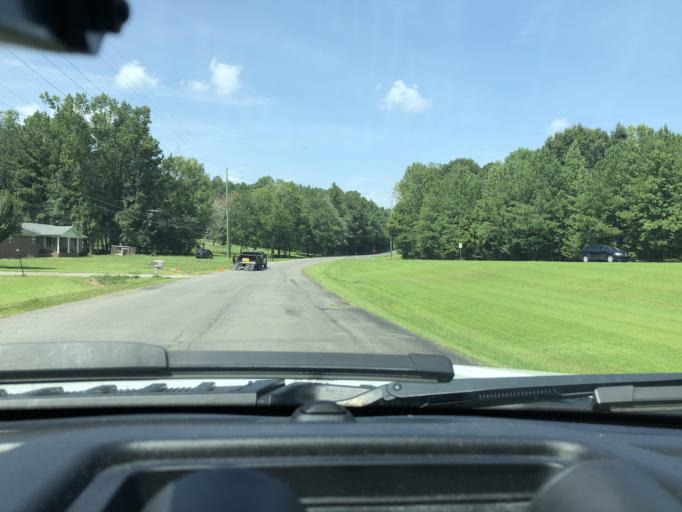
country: US
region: Georgia
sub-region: Whitfield County
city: Dalton
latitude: 34.7340
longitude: -84.9361
